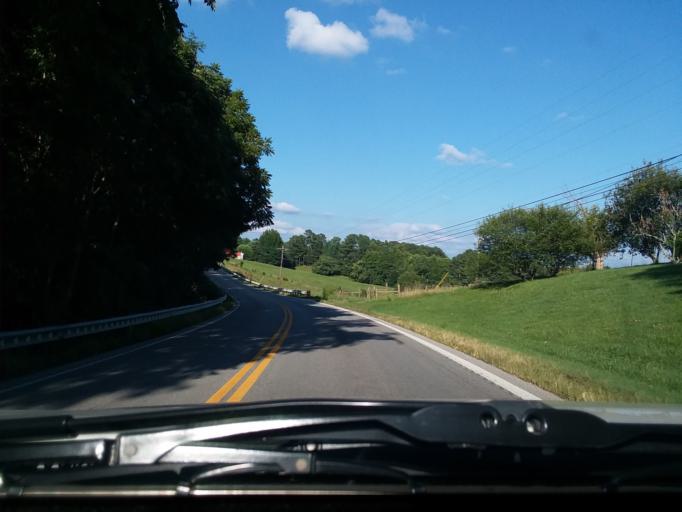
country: US
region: Tennessee
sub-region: Clay County
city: Celina
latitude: 36.5929
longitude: -85.5926
